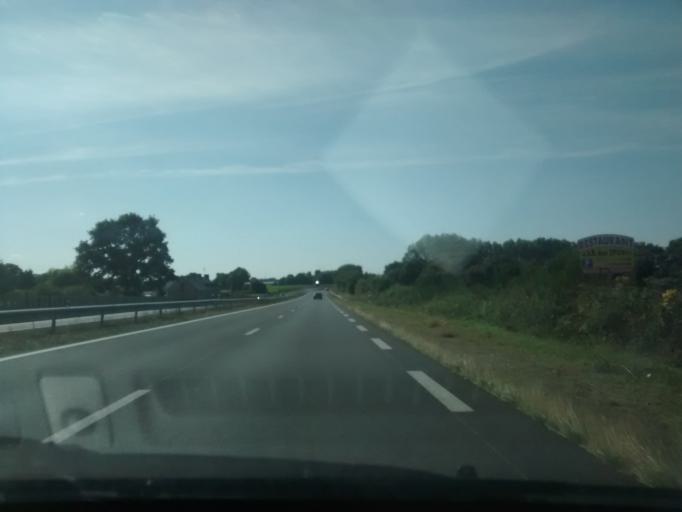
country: FR
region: Brittany
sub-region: Departement des Cotes-d'Armor
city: Pedernec
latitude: 48.5830
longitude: -3.2413
